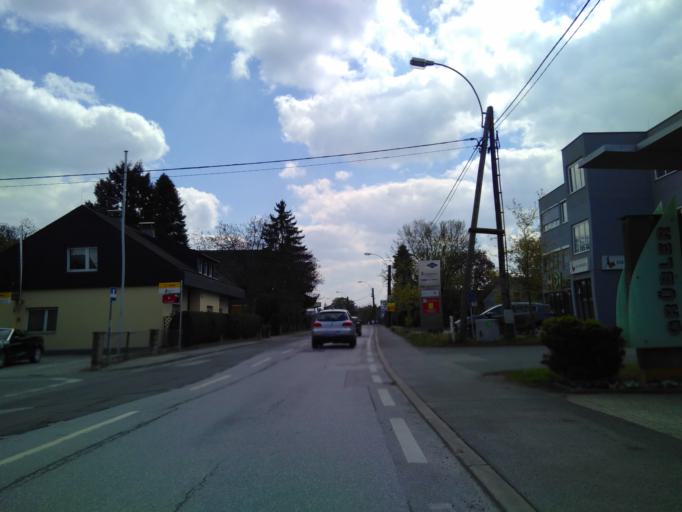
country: AT
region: Styria
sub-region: Politischer Bezirk Graz-Umgebung
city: Feldkirchen bei Graz
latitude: 47.0261
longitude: 15.4675
